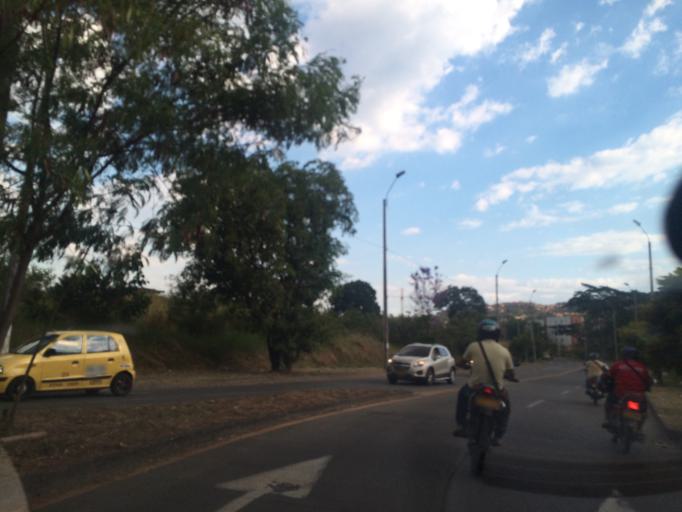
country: CO
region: Valle del Cauca
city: Cali
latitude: 3.3985
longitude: -76.5567
